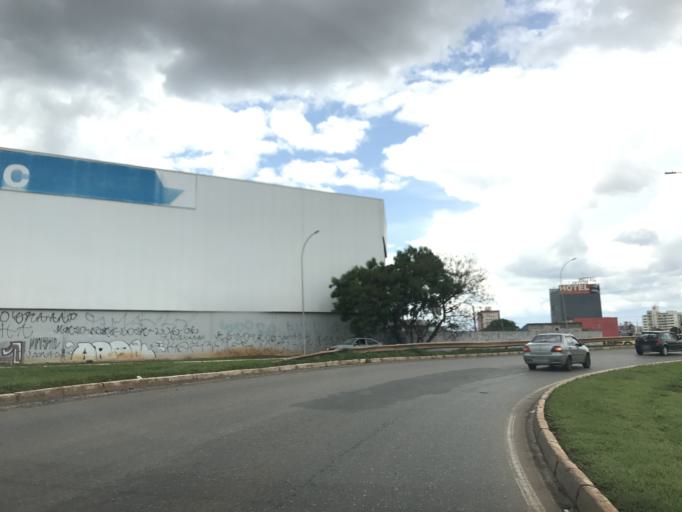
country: BR
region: Federal District
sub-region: Brasilia
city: Brasilia
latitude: -15.8822
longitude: -48.0618
